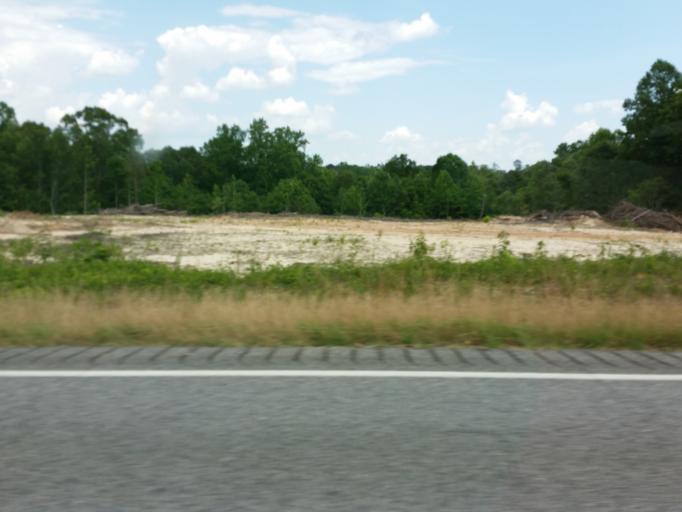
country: US
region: Alabama
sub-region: Sumter County
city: York
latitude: 32.3754
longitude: -88.1950
